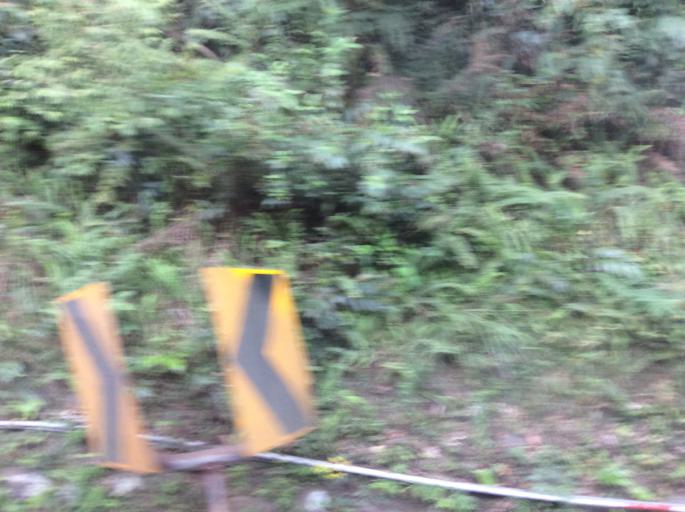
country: TW
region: Taipei
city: Taipei
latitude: 25.1657
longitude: 121.5433
